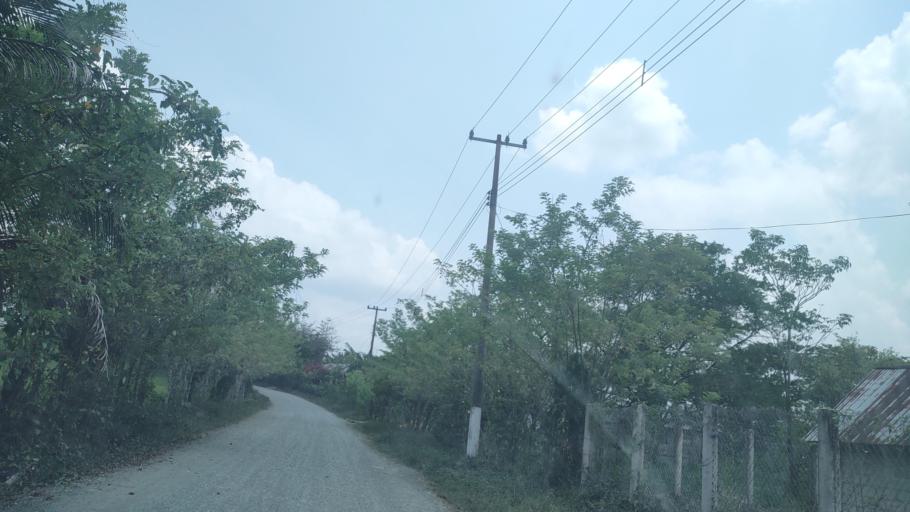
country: MX
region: Tabasco
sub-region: Huimanguillo
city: Francisco Rueda
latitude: 17.5864
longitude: -93.9588
